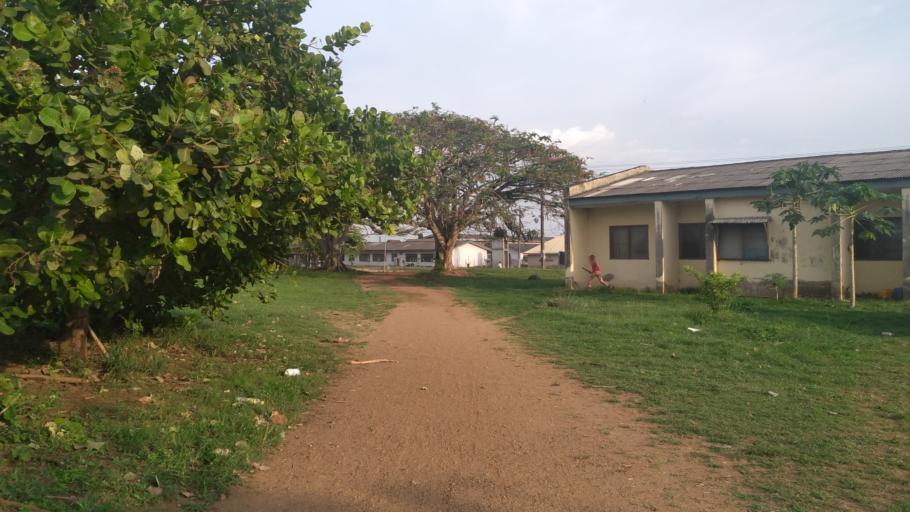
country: NG
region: Ondo
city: Ilare
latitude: 7.2970
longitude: 5.1473
